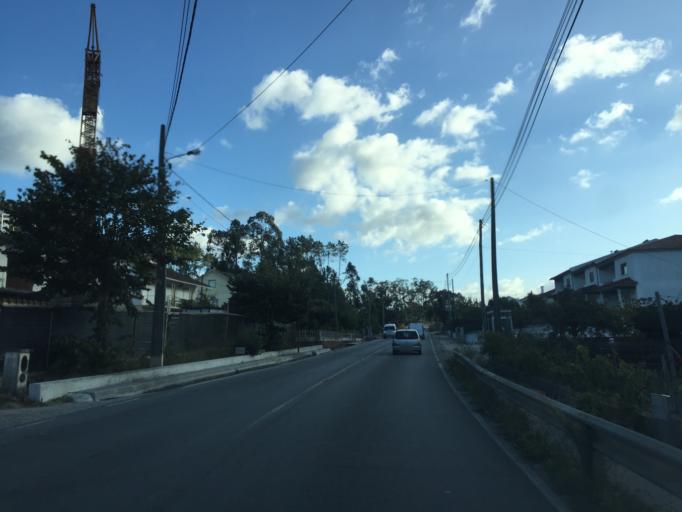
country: PT
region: Leiria
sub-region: Leiria
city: Souto da Carpalhosa
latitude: 39.8584
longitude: -8.8352
